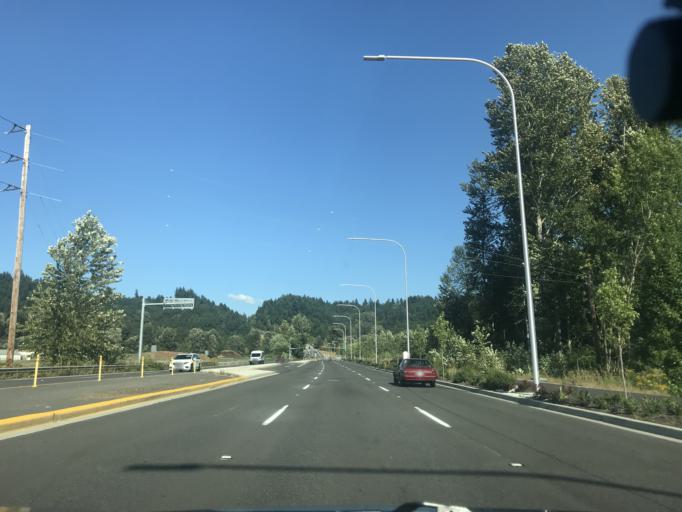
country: US
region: Washington
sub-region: King County
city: Kent
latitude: 47.3536
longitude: -122.2197
